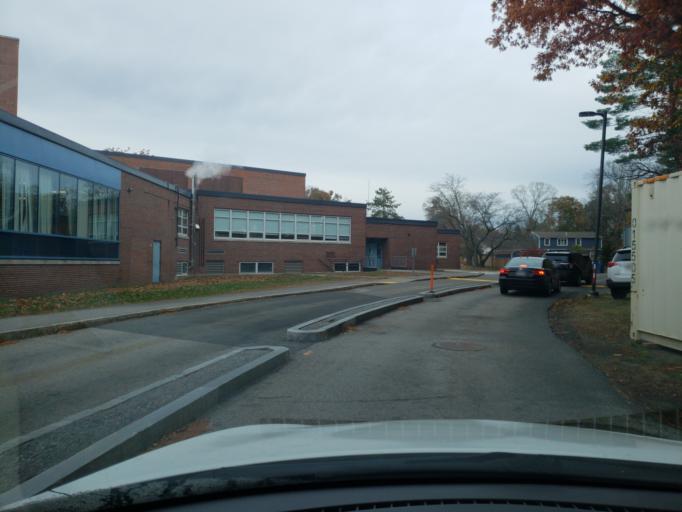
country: US
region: Massachusetts
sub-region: Essex County
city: Andover
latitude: 42.6583
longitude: -71.1517
